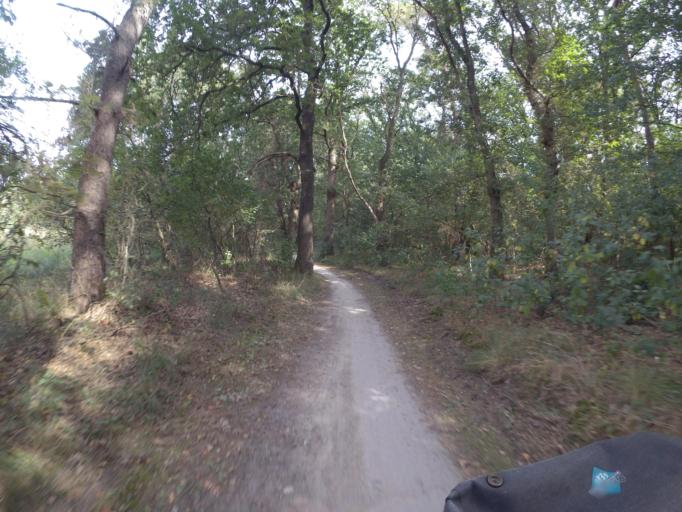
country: NL
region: Drenthe
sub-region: Gemeente Westerveld
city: Havelte
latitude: 52.8191
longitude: 6.2730
